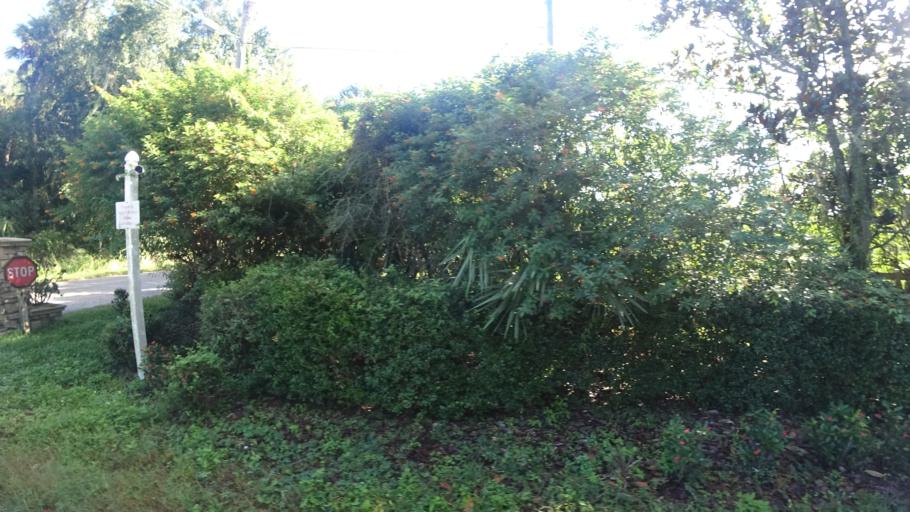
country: US
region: Florida
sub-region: Manatee County
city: Ellenton
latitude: 27.5829
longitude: -82.5089
